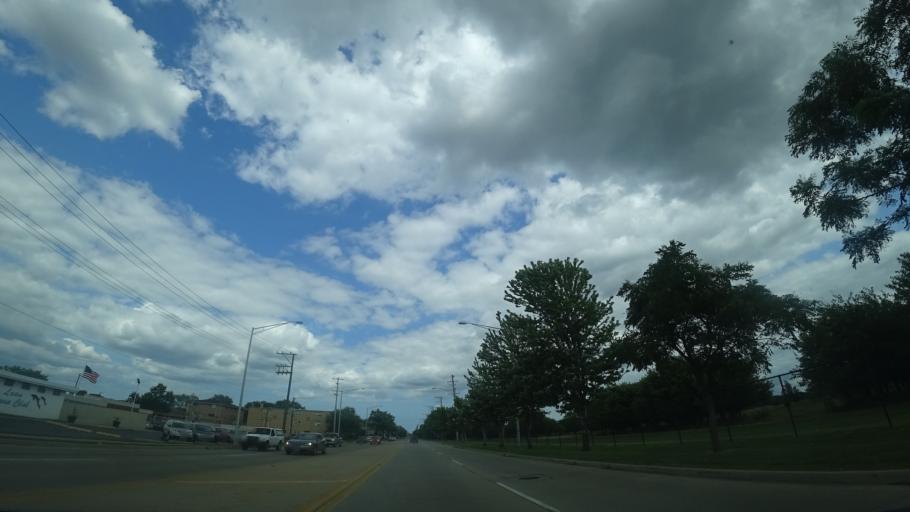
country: US
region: Illinois
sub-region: Cook County
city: Alsip
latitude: 41.6910
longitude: -87.7344
